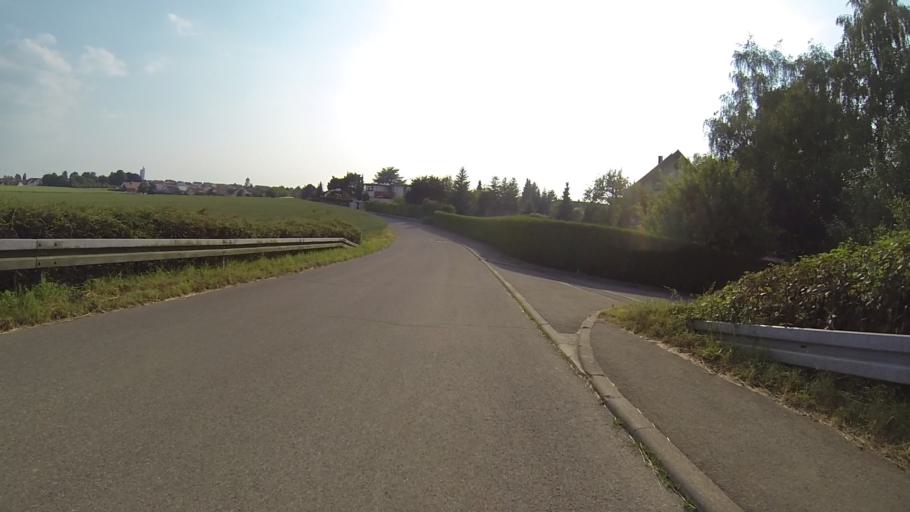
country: DE
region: Baden-Wuerttemberg
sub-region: Tuebingen Region
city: Beimerstetten
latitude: 48.4491
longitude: 9.9982
